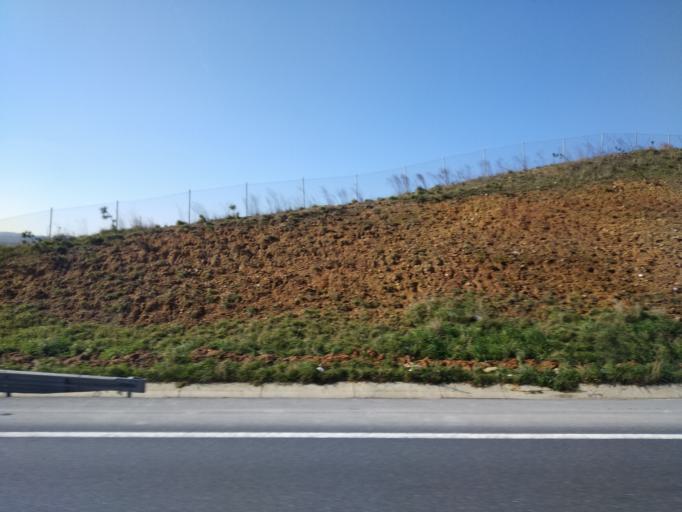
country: TR
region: Istanbul
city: Mahmut Sevket Pasa
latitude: 41.1335
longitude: 29.2867
